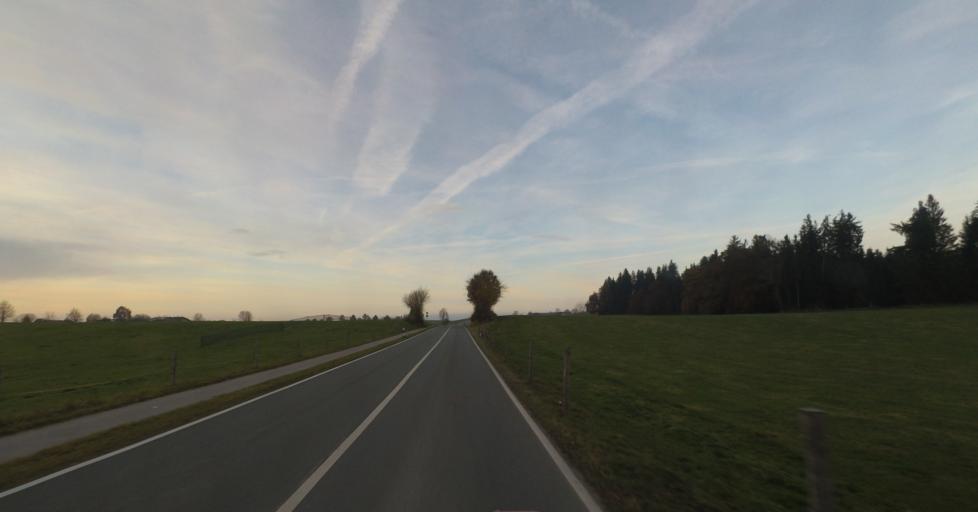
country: DE
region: Bavaria
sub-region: Upper Bavaria
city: Gstadt am Chiemsee
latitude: 47.8971
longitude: 12.3934
